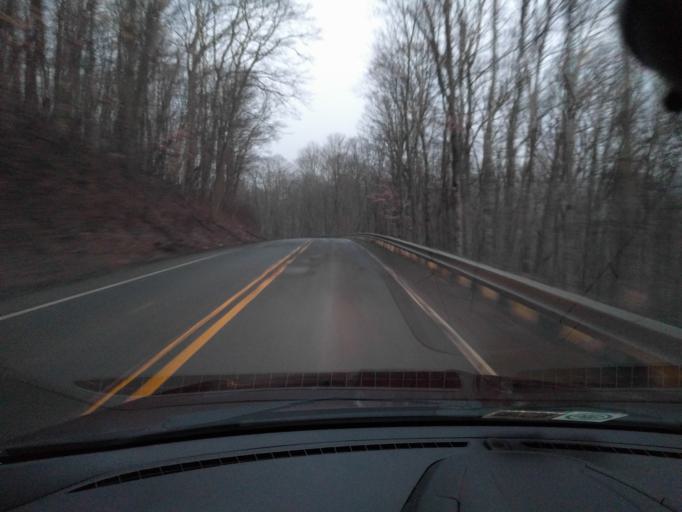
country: US
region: West Virginia
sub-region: Greenbrier County
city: Rainelle
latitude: 37.9825
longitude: -80.8329
